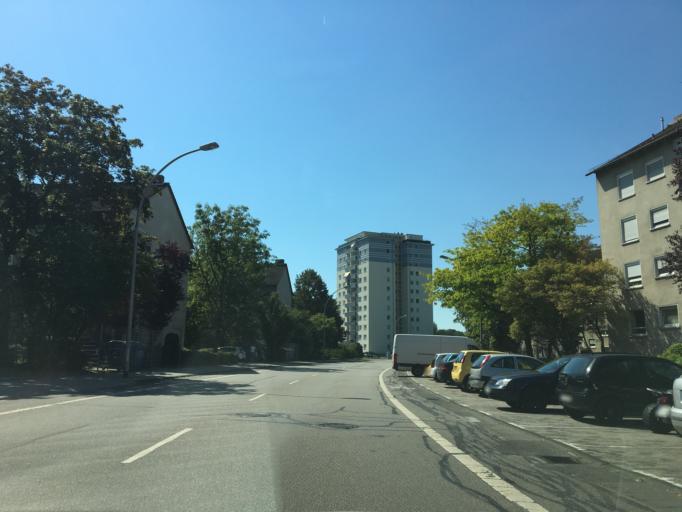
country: DE
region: Hesse
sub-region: Regierungsbezirk Darmstadt
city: Russelsheim
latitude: 49.9843
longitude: 8.4498
